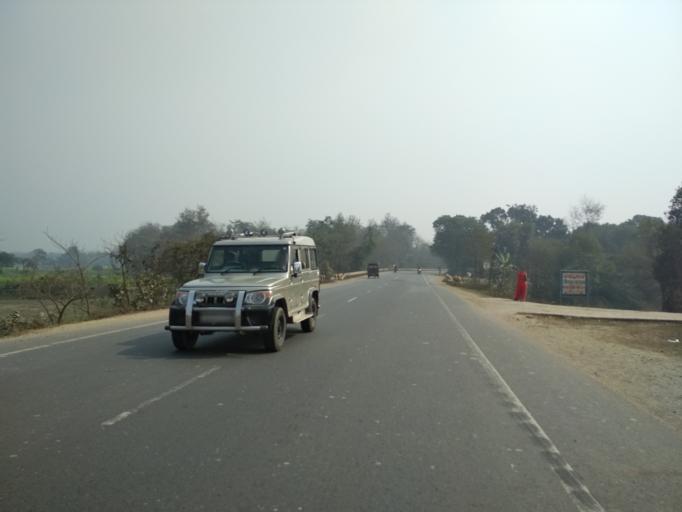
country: IN
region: Bihar
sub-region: Khagaria
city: Khagaria
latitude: 25.5060
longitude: 86.5866
